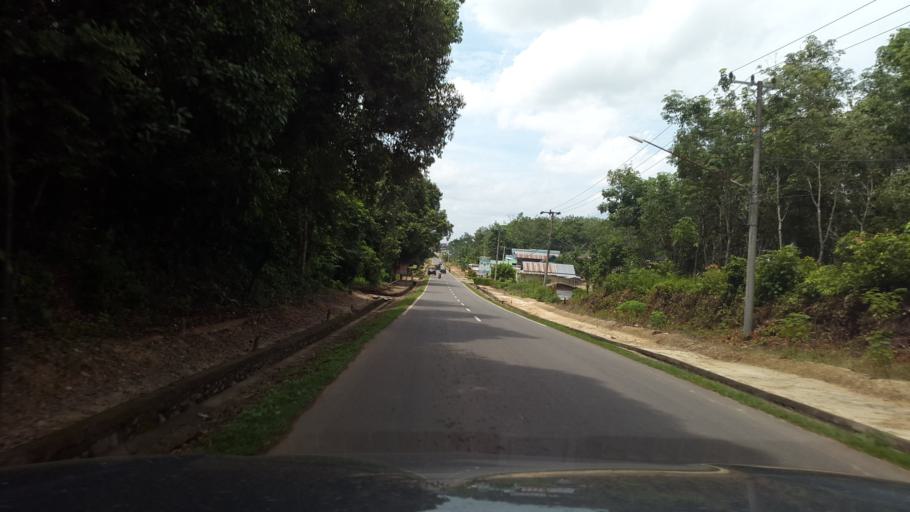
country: ID
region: South Sumatra
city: Gunungmegang Dalam
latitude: -3.3139
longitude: 103.8887
